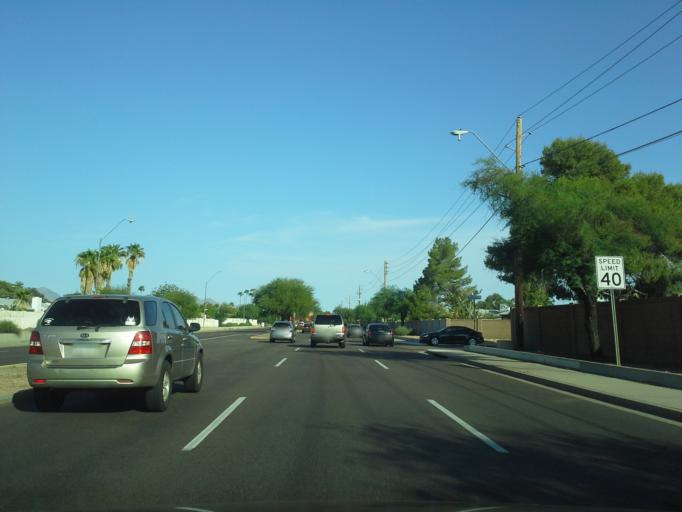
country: US
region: Arizona
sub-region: Maricopa County
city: Paradise Valley
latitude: 33.5971
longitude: -111.9989
